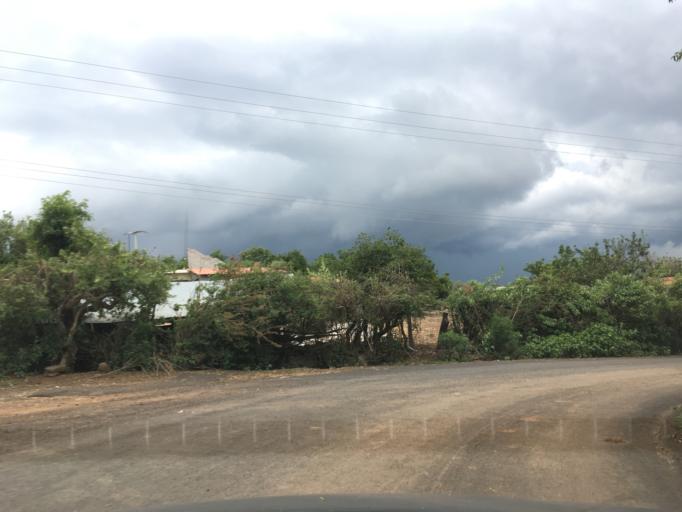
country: MX
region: Michoacan
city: Acuitzio del Canje
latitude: 19.5563
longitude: -101.2749
